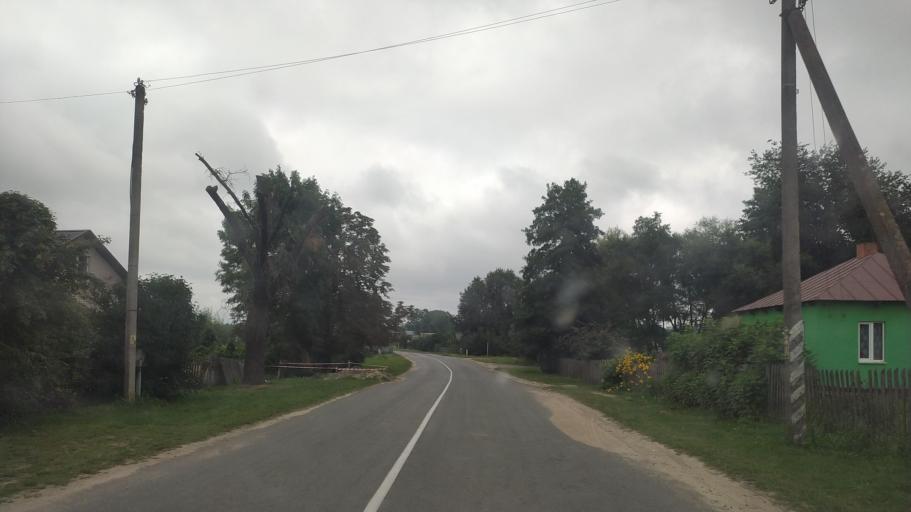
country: BY
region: Brest
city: Byaroza
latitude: 52.5919
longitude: 24.8709
